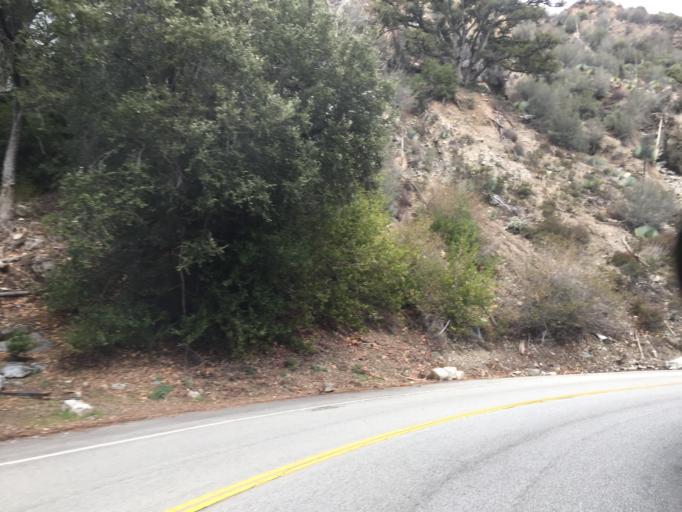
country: US
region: California
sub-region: Los Angeles County
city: Glendora
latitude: 34.3013
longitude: -117.8382
